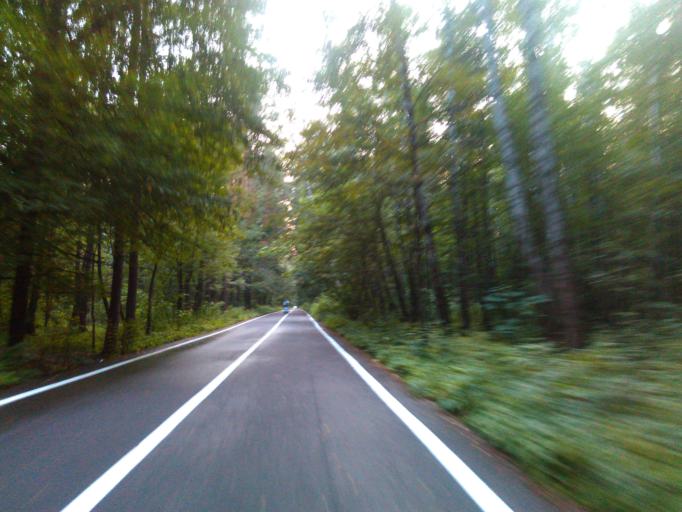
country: RU
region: Moscow
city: Babushkin
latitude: 55.8653
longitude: 37.7183
